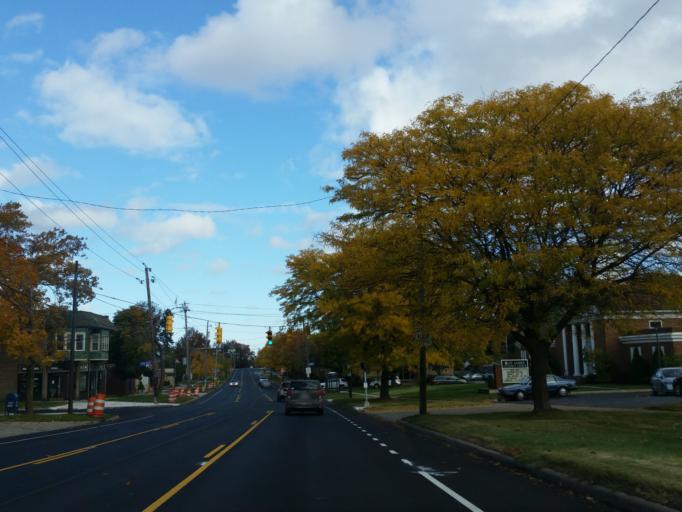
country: US
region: Ohio
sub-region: Cuyahoga County
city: Brooklyn Heights
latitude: 41.4261
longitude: -81.6969
